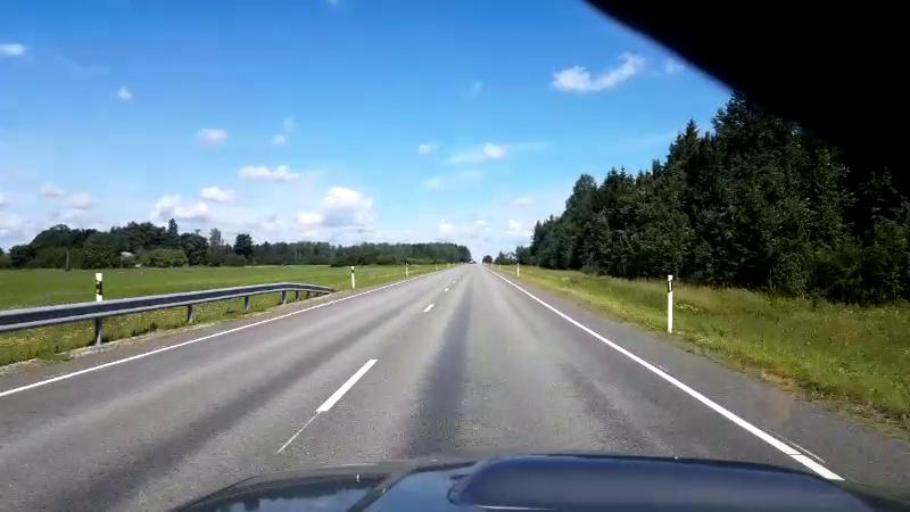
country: EE
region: Jaervamaa
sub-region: Jaerva-Jaani vald
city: Jarva-Jaani
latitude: 59.1571
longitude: 25.7653
